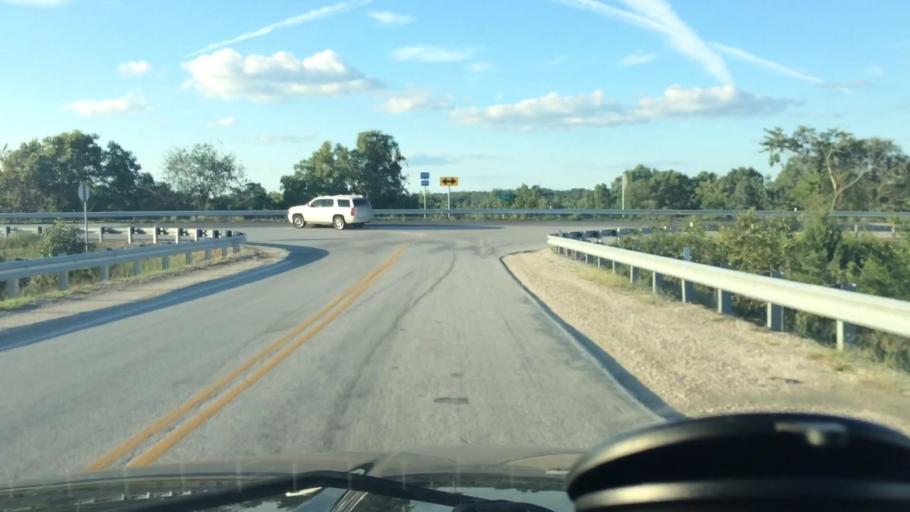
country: US
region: Missouri
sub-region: Webster County
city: Marshfield
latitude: 37.3023
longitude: -92.9994
